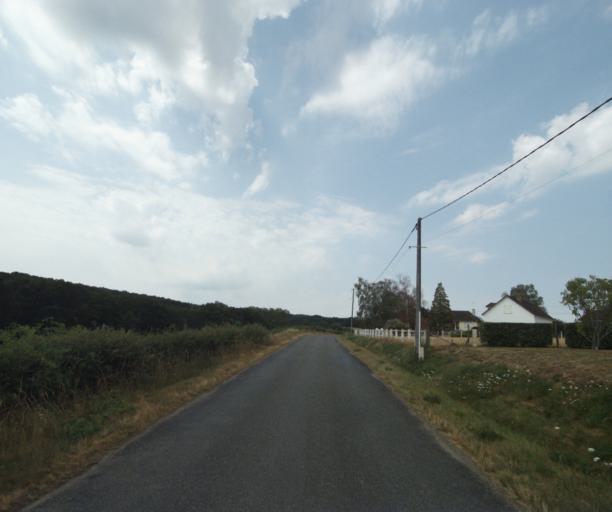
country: FR
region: Bourgogne
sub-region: Departement de Saone-et-Loire
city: Gueugnon
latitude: 46.5874
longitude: 4.0280
